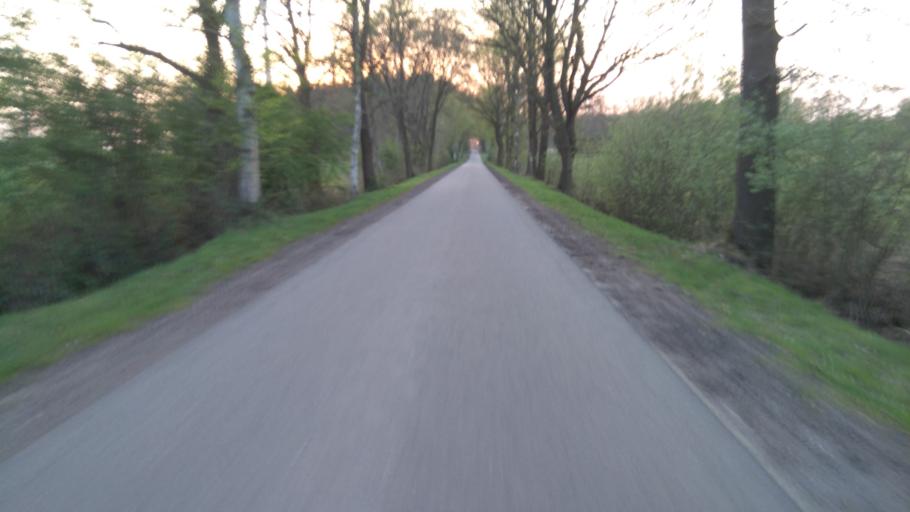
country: DE
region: Lower Saxony
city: Harsefeld
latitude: 53.4919
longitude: 9.4985
